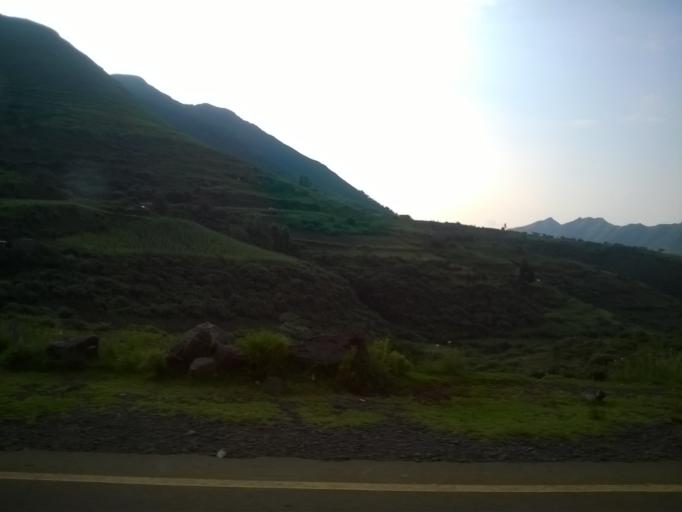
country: LS
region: Butha-Buthe
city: Butha-Buthe
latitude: -29.0466
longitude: 28.3134
